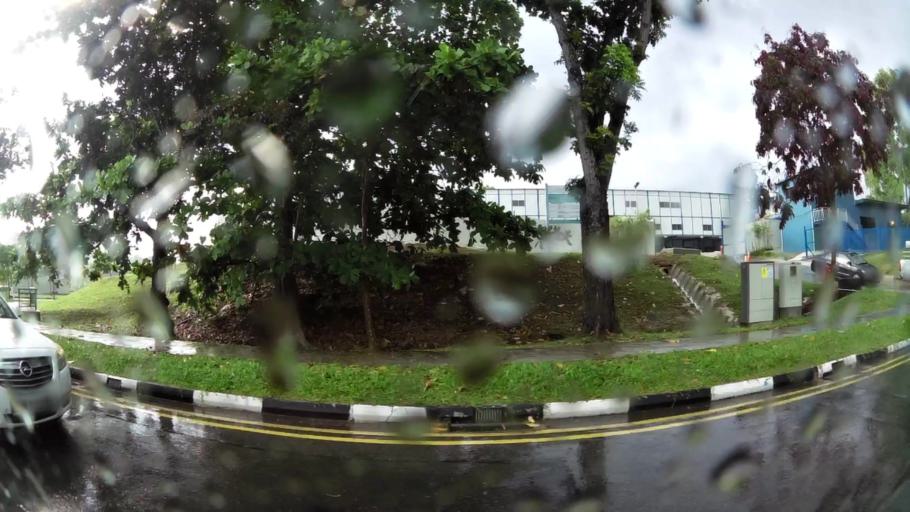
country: SG
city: Singapore
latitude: 1.3365
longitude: 103.9588
